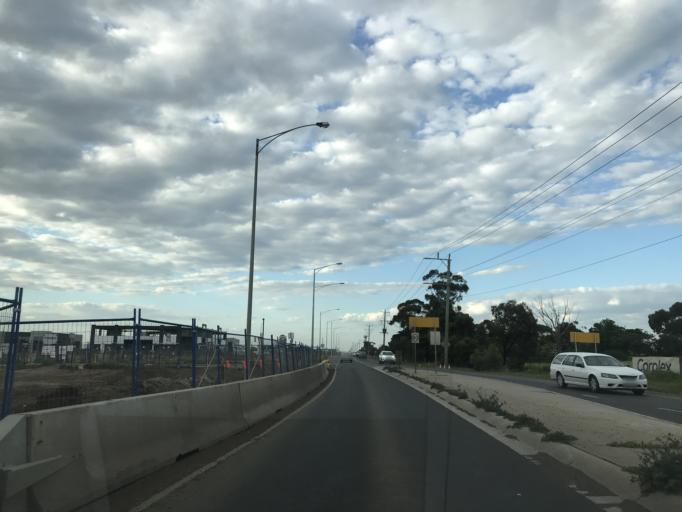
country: AU
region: Victoria
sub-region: Wyndham
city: Truganina
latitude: -37.8382
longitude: 144.7471
